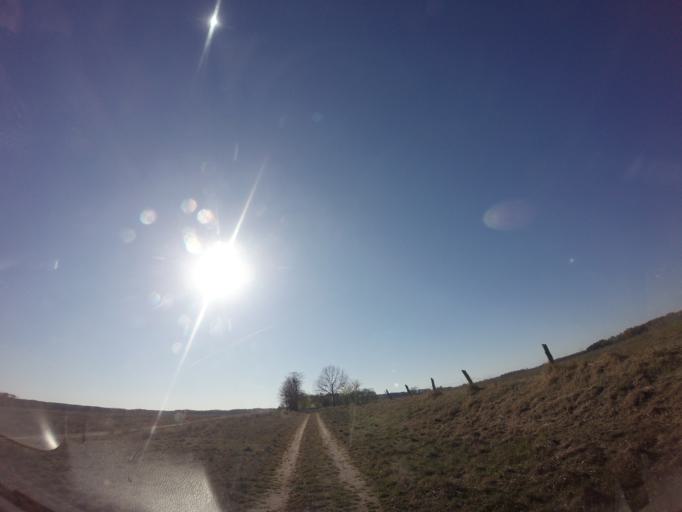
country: PL
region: West Pomeranian Voivodeship
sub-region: Powiat choszczenski
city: Drawno
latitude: 53.2423
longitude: 15.6563
